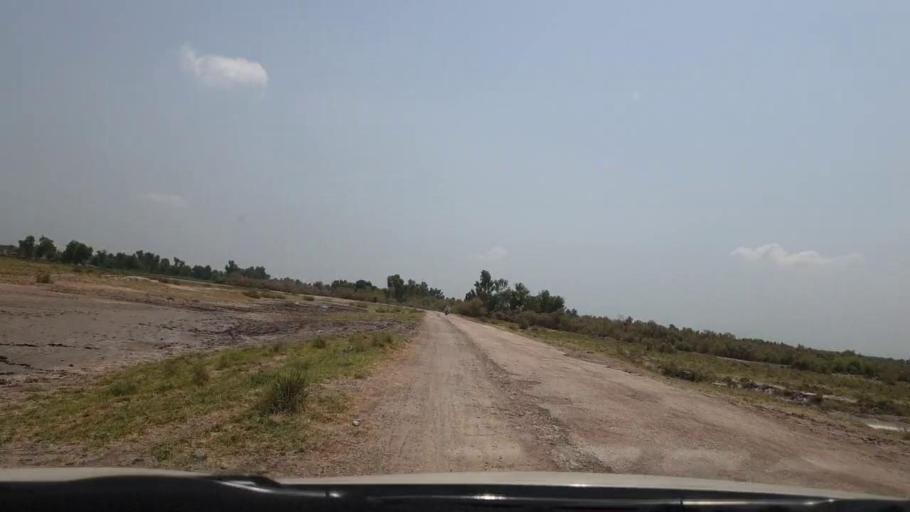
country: PK
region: Sindh
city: New Badah
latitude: 27.2986
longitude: 68.0651
